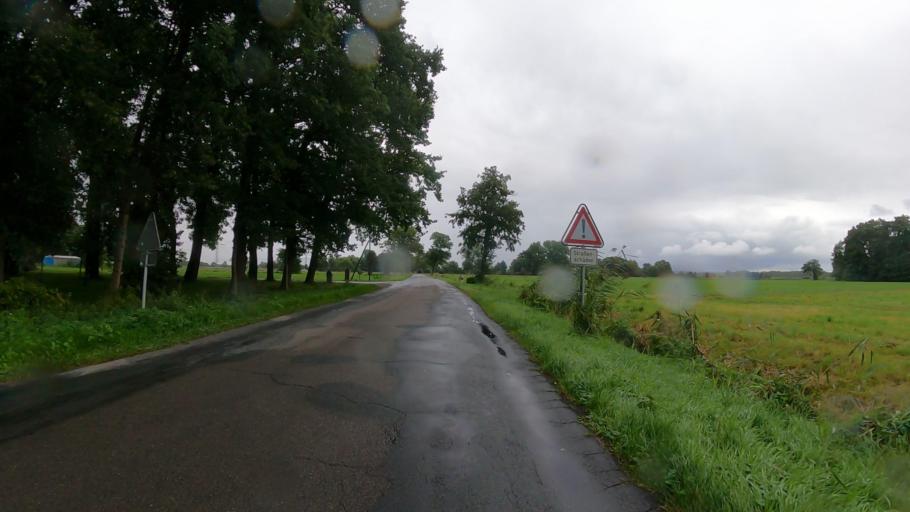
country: DE
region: Lower Saxony
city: Buxtehude
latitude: 53.4830
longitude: 9.7415
